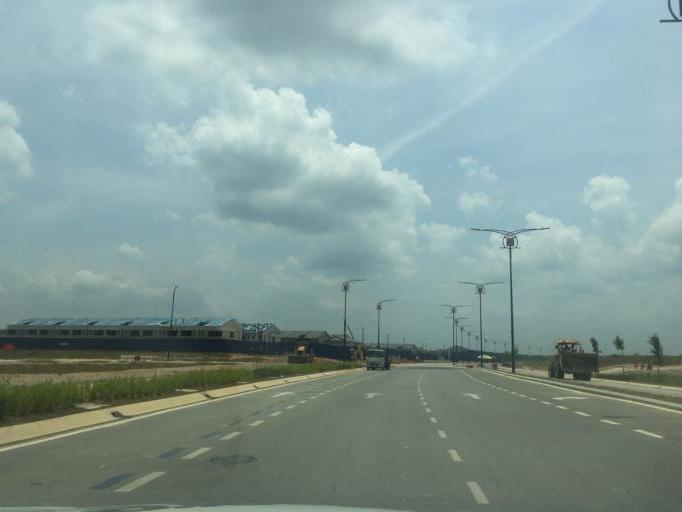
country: MY
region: Putrajaya
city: Putrajaya
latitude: 2.8483
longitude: 101.7055
